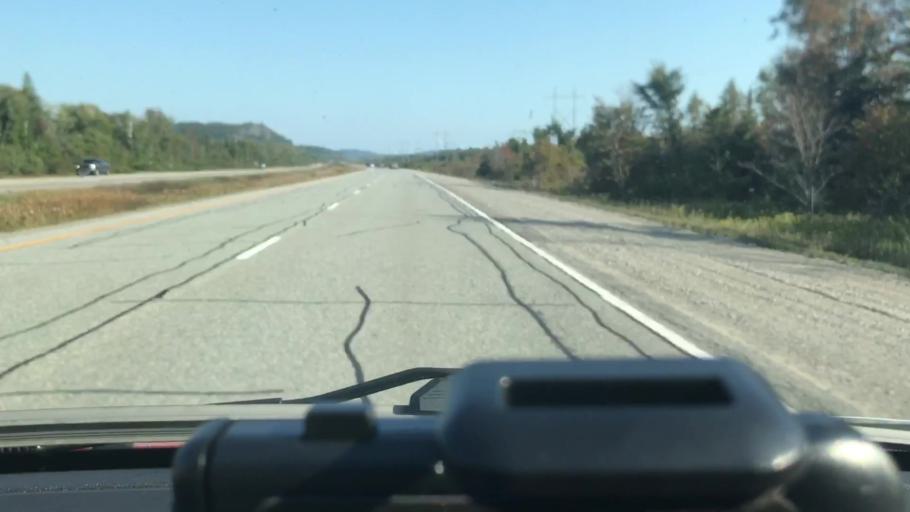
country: CA
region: Ontario
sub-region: Algoma
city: Sault Ste. Marie
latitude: 46.5398
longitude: -84.1280
